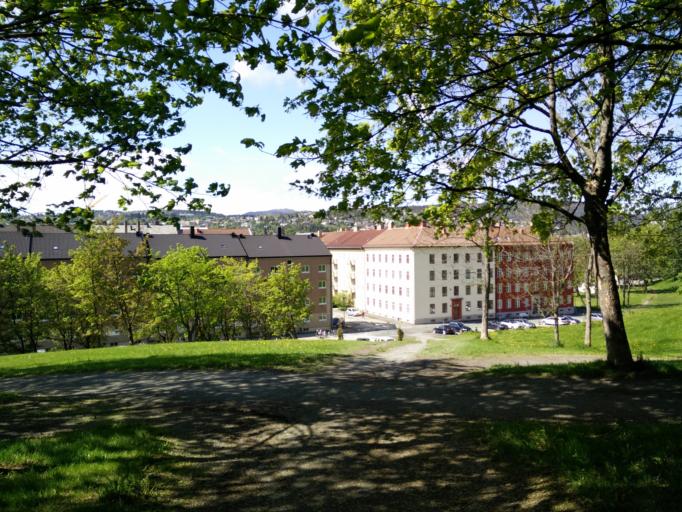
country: NO
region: Sor-Trondelag
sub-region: Trondheim
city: Trondheim
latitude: 63.4164
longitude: 10.4020
